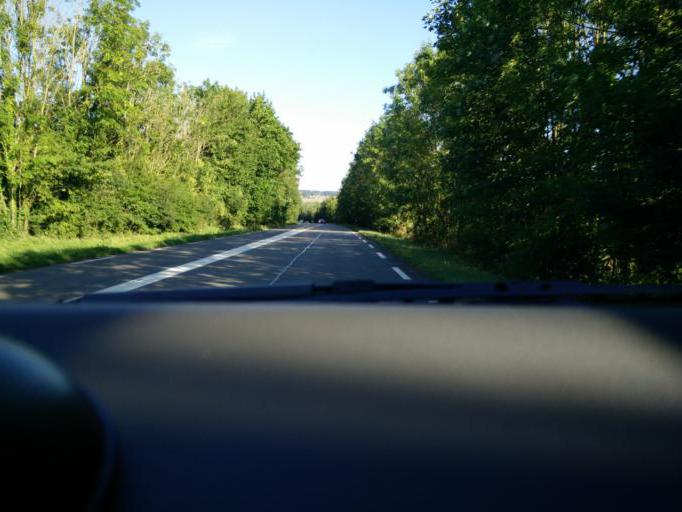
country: FR
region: Nord-Pas-de-Calais
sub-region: Departement du Pas-de-Calais
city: Houdain
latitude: 50.4654
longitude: 2.5331
